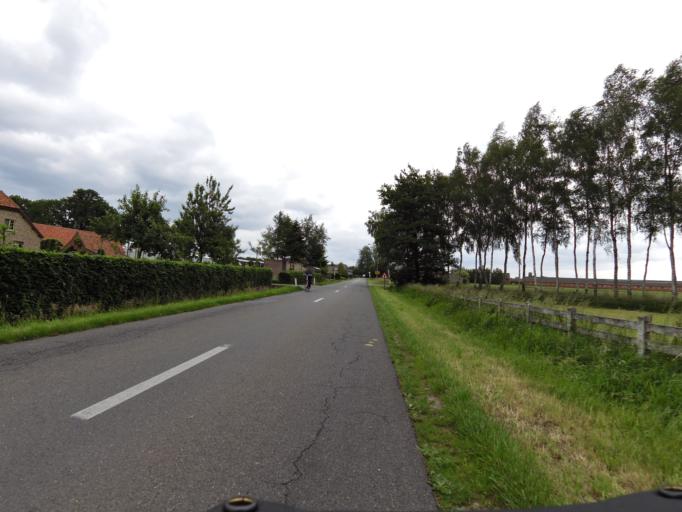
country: BE
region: Flanders
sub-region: Provincie Antwerpen
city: Hoogstraten
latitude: 51.4871
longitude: 4.7844
